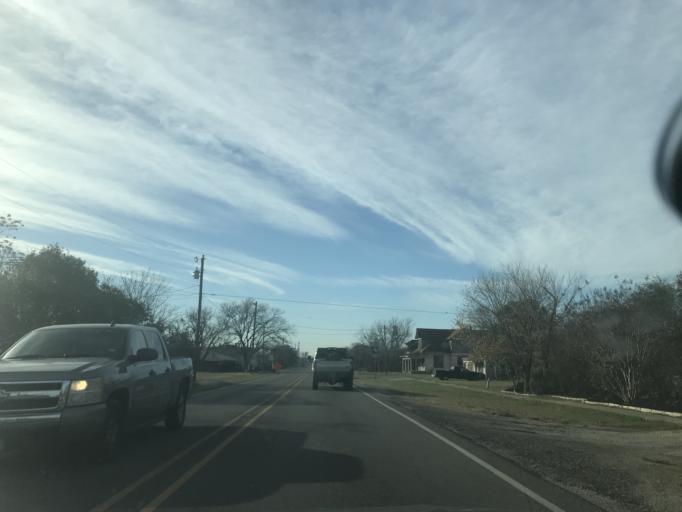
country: US
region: Texas
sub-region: Travis County
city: Manor
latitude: 30.3455
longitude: -97.5567
